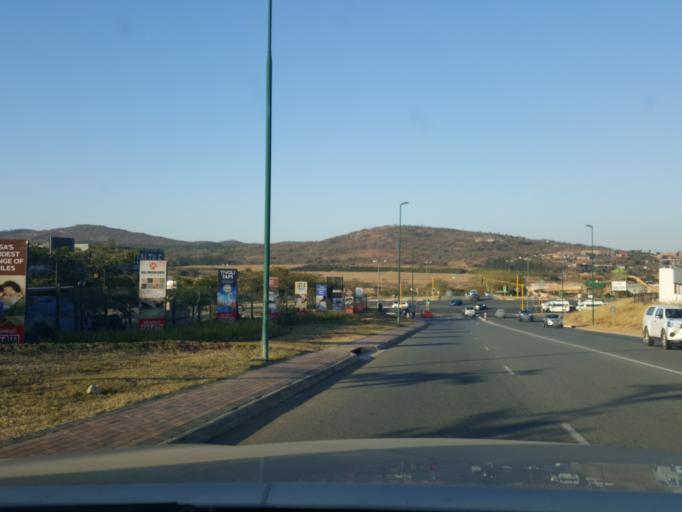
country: ZA
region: Mpumalanga
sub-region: Ehlanzeni District
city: Nelspruit
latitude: -25.4357
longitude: 30.9638
